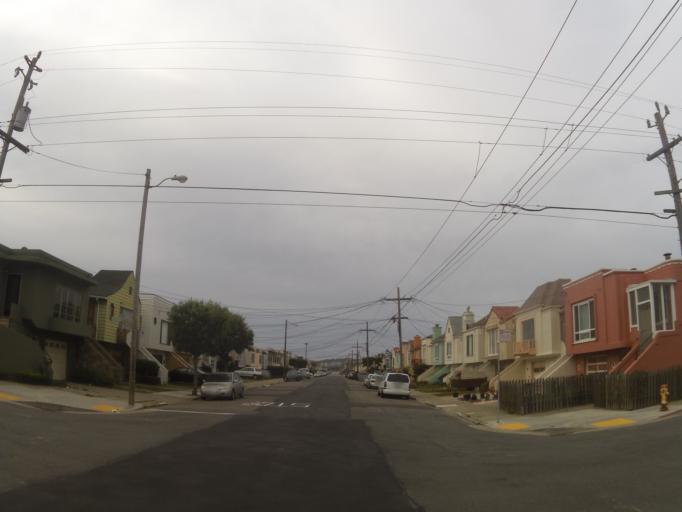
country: US
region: California
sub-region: San Mateo County
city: Daly City
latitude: 37.7473
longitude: -122.5061
